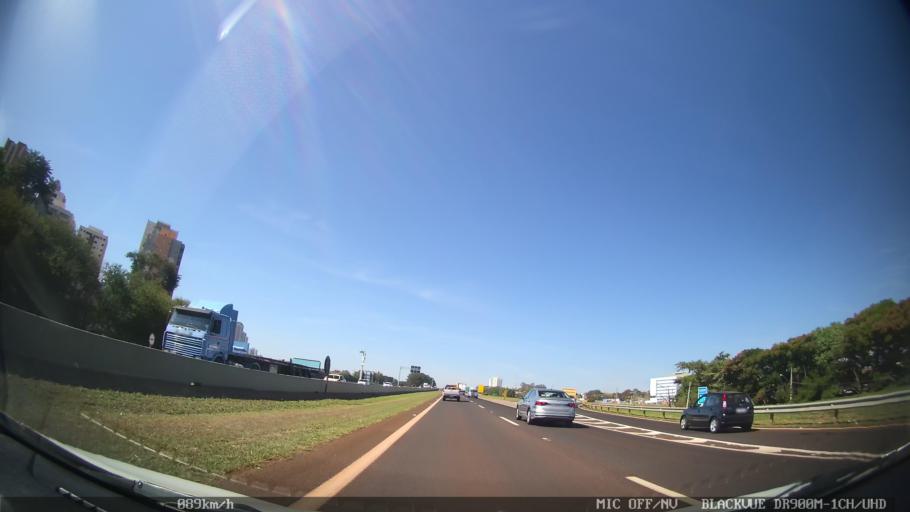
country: BR
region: Sao Paulo
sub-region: Ribeirao Preto
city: Ribeirao Preto
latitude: -21.2222
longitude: -47.8197
